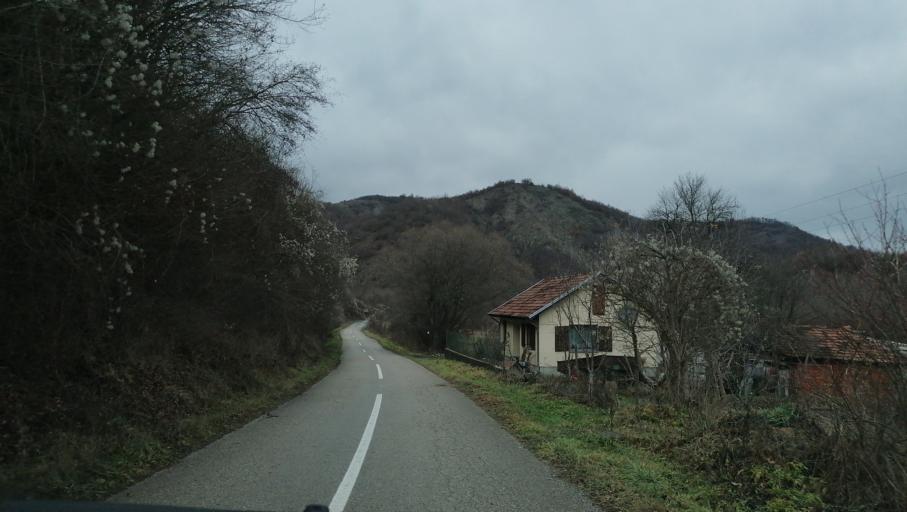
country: RS
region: Central Serbia
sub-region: Pirotski Okrug
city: Dimitrovgrad
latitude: 42.9451
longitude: 22.7674
